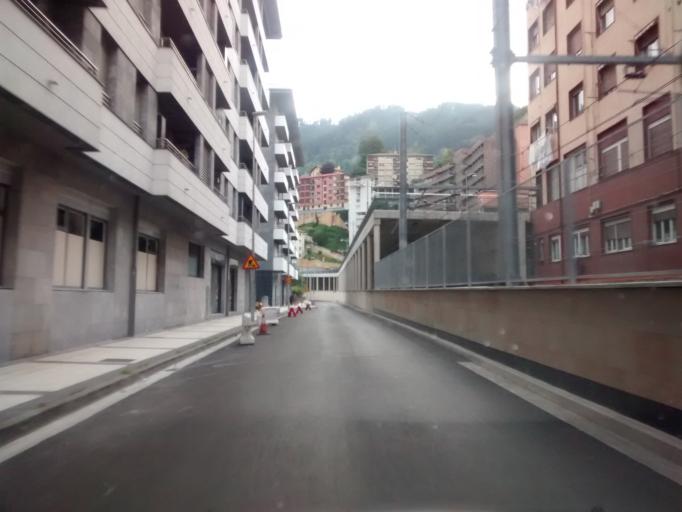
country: ES
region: Basque Country
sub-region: Provincia de Guipuzcoa
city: Eibar
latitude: 43.1844
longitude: -2.4765
